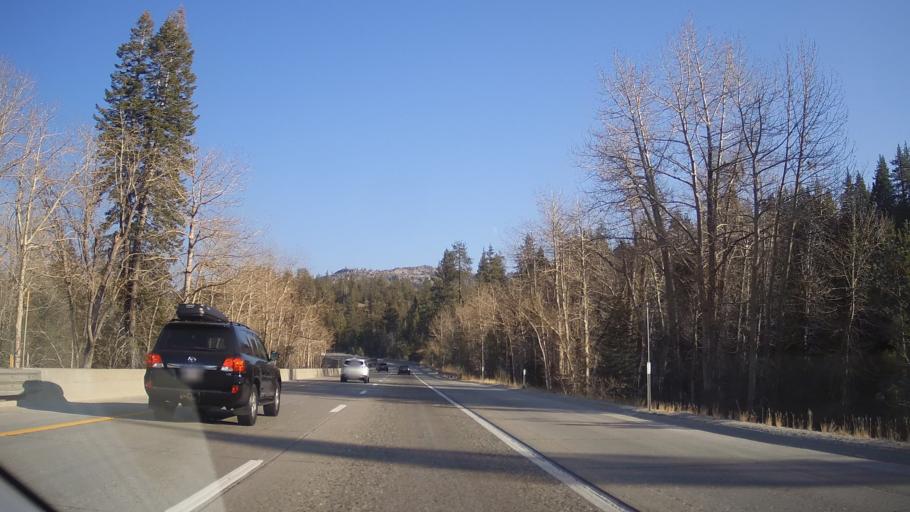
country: US
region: California
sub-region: Nevada County
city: Truckee
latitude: 39.3047
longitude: -120.5354
